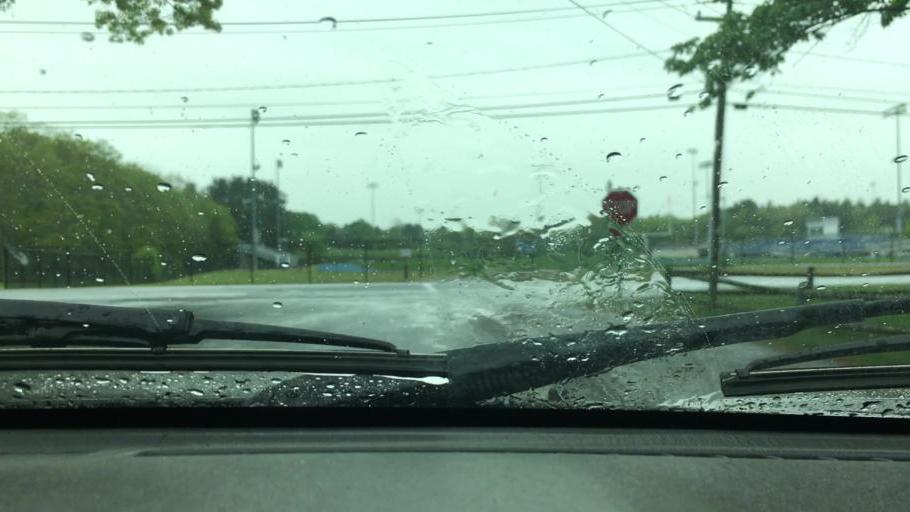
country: US
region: Massachusetts
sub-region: Franklin County
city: Turners Falls
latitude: 42.5889
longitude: -72.5404
